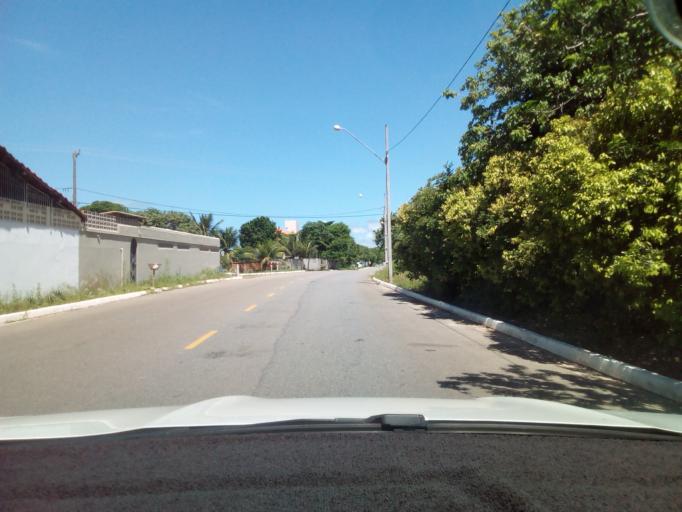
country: BR
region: Paraiba
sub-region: Joao Pessoa
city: Joao Pessoa
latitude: -7.1550
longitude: -34.7954
